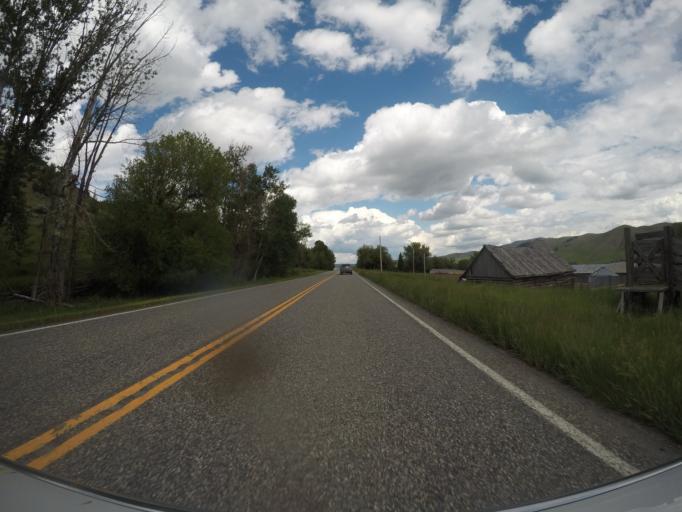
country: US
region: Montana
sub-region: Sweet Grass County
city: Big Timber
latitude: 45.6850
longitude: -110.0811
